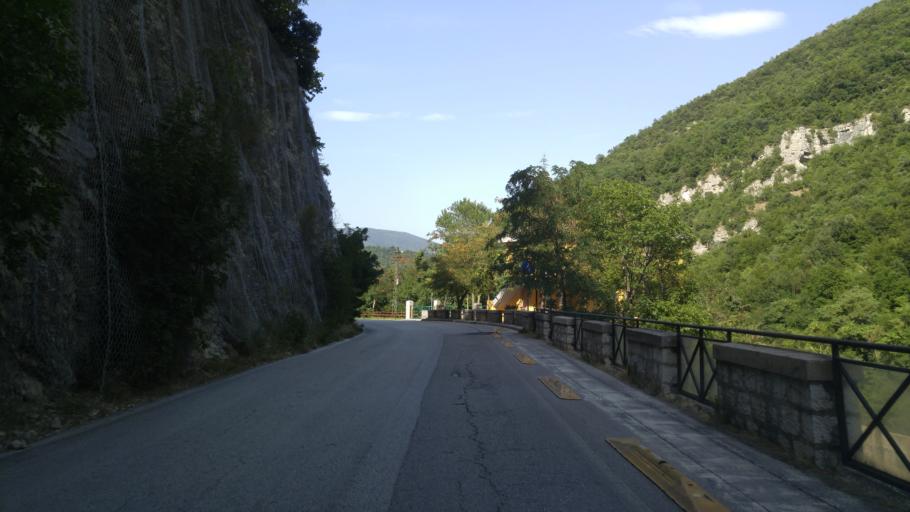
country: IT
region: The Marches
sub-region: Provincia di Pesaro e Urbino
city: Canavaccio
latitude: 43.6547
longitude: 12.7326
